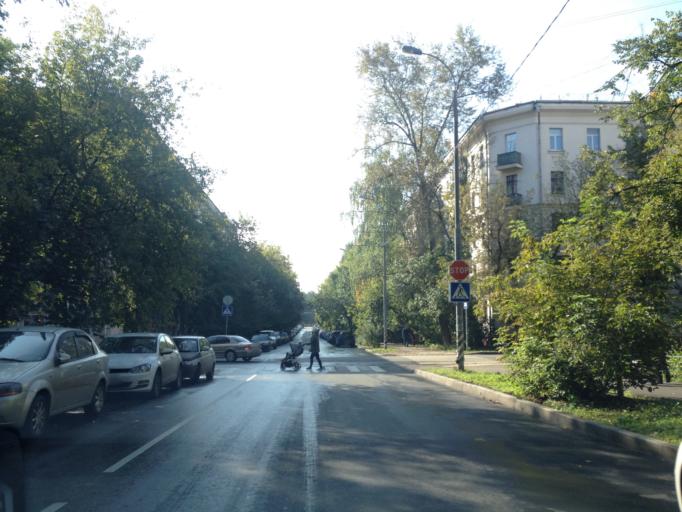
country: RU
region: Moskovskaya
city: Izmaylovo
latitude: 55.7913
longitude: 37.7941
